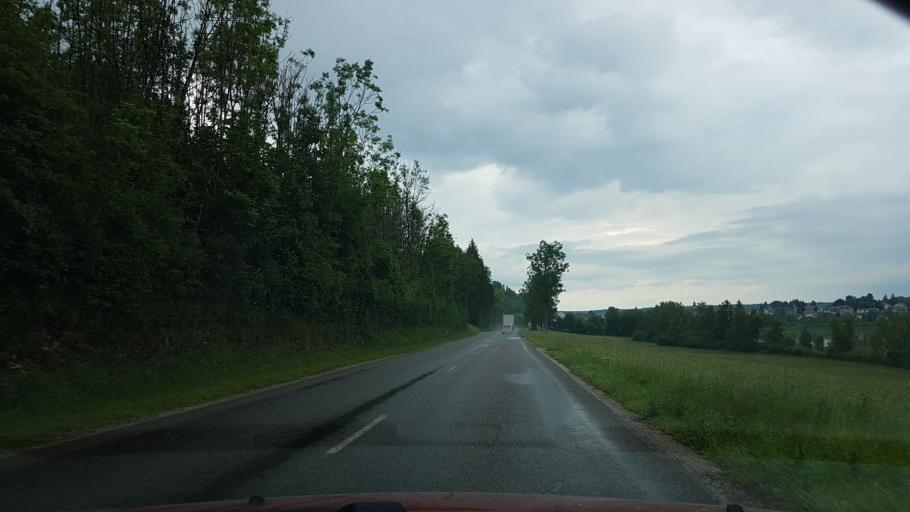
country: FR
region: Franche-Comte
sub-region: Departement du Jura
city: Clairvaux-les-Lacs
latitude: 46.5652
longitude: 5.7441
